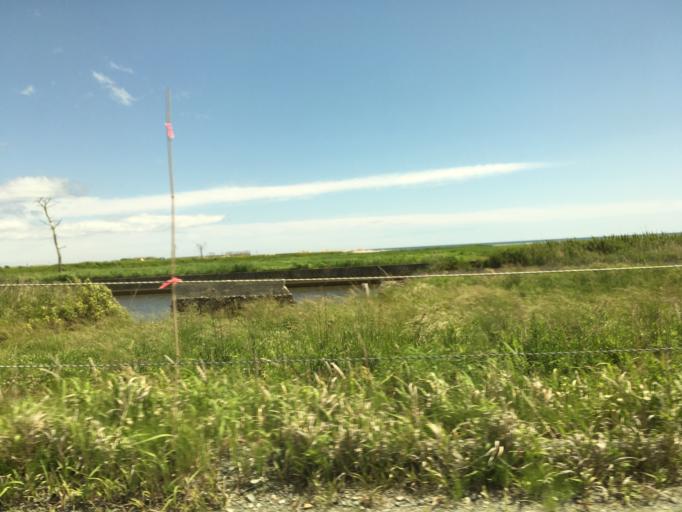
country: JP
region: Fukushima
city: Namie
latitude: 37.4588
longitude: 141.0323
